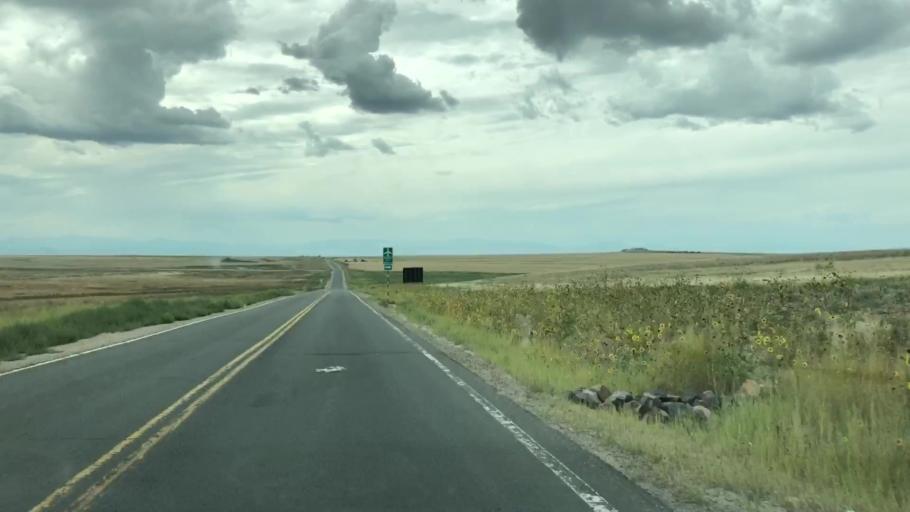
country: US
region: Colorado
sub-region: Adams County
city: Aurora
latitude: 39.7984
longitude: -104.6877
